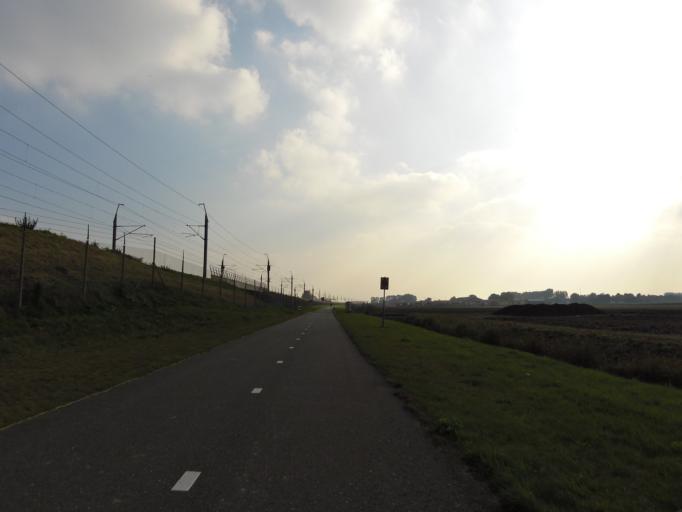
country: NL
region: South Holland
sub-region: Gemeente Rijnwoude
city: Benthuizen
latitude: 52.0844
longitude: 4.5650
